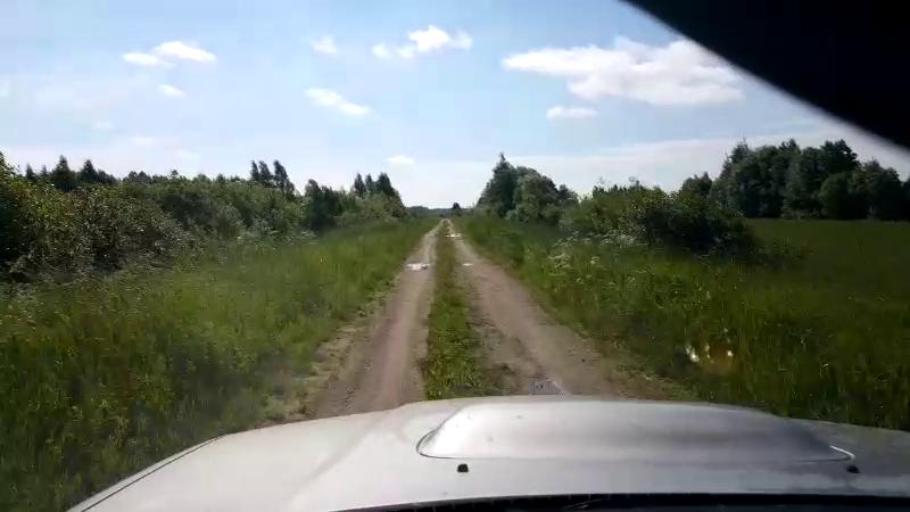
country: EE
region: Paernumaa
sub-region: Sindi linn
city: Sindi
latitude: 58.4992
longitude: 24.6504
